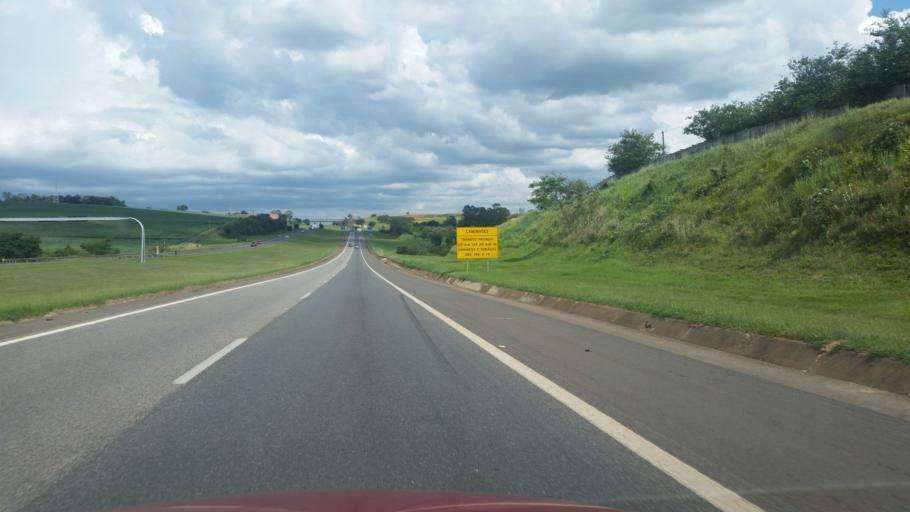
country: BR
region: Sao Paulo
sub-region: Tatui
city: Tatui
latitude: -23.2787
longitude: -47.8189
